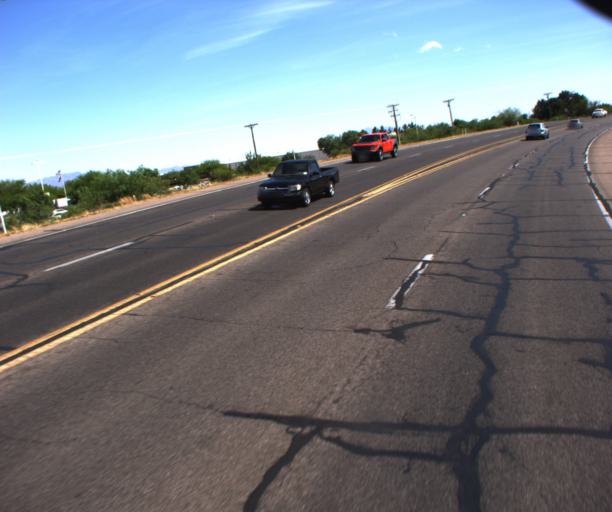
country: US
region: Arizona
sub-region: Cochise County
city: Sierra Vista
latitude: 31.5671
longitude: -110.2578
